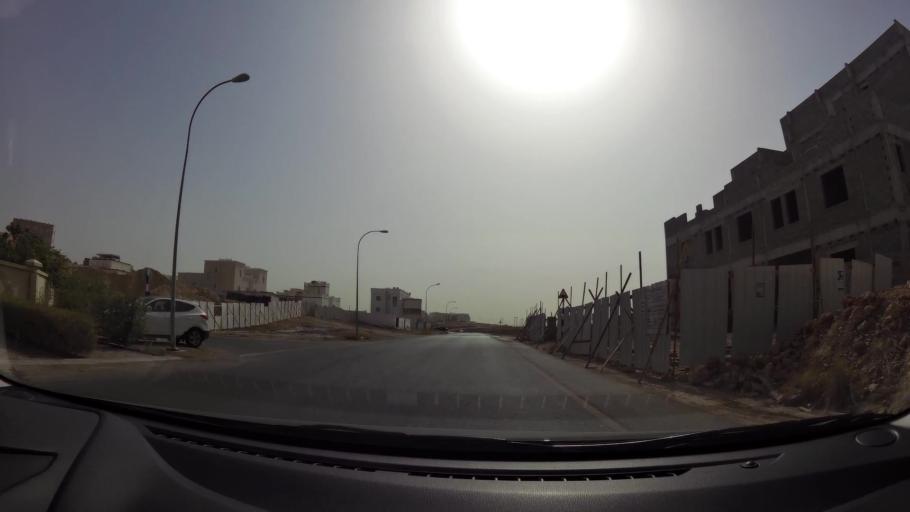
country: OM
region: Muhafazat Masqat
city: Bawshar
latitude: 23.5605
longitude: 58.3566
